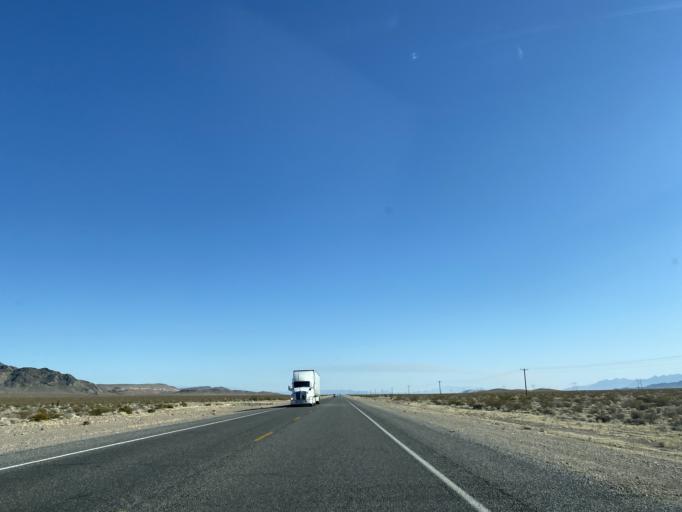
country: US
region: Nevada
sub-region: Nye County
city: Beatty
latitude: 36.7527
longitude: -116.6594
